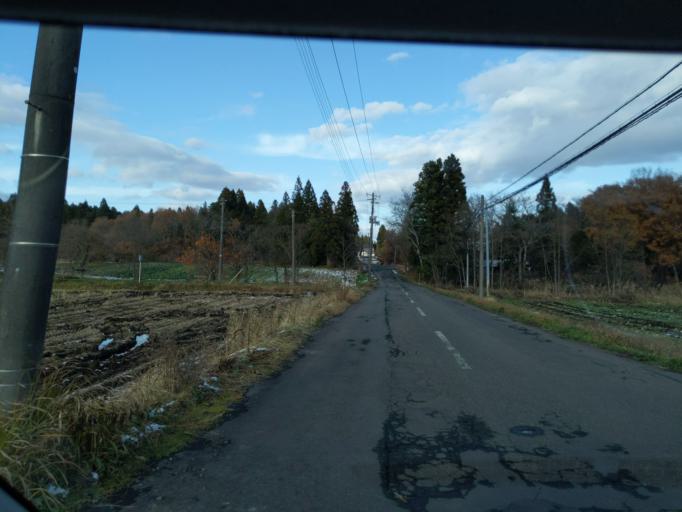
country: JP
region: Iwate
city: Kitakami
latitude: 39.2319
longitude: 141.0498
